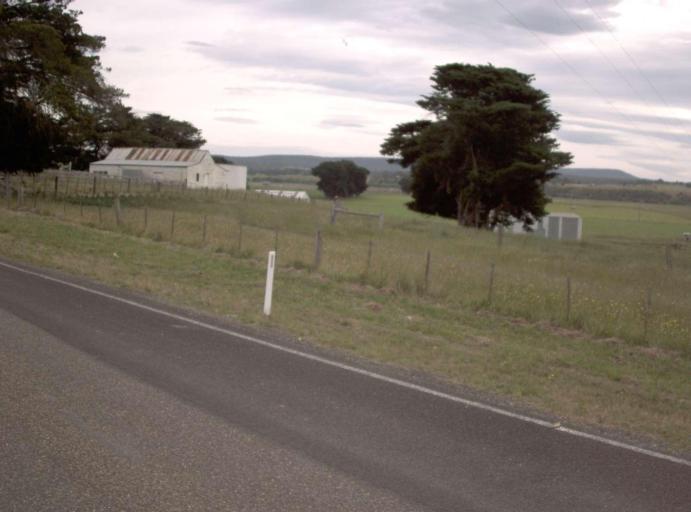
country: AU
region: Victoria
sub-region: East Gippsland
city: Bairnsdale
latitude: -37.8106
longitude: 147.4857
